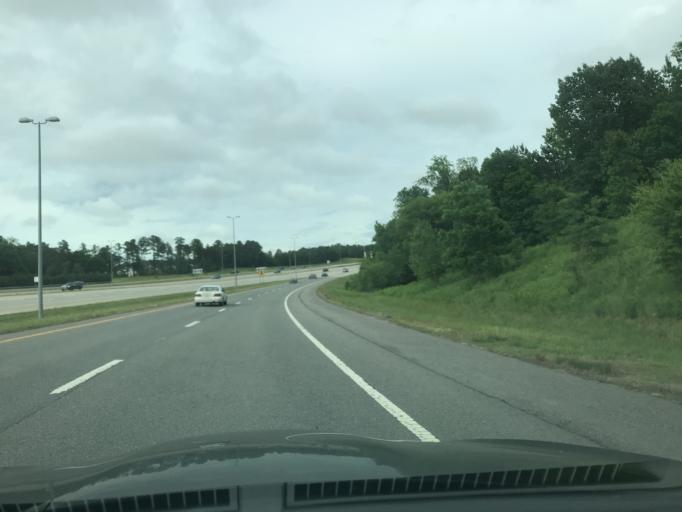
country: US
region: North Carolina
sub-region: Wake County
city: Morrisville
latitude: 35.8572
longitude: -78.8562
